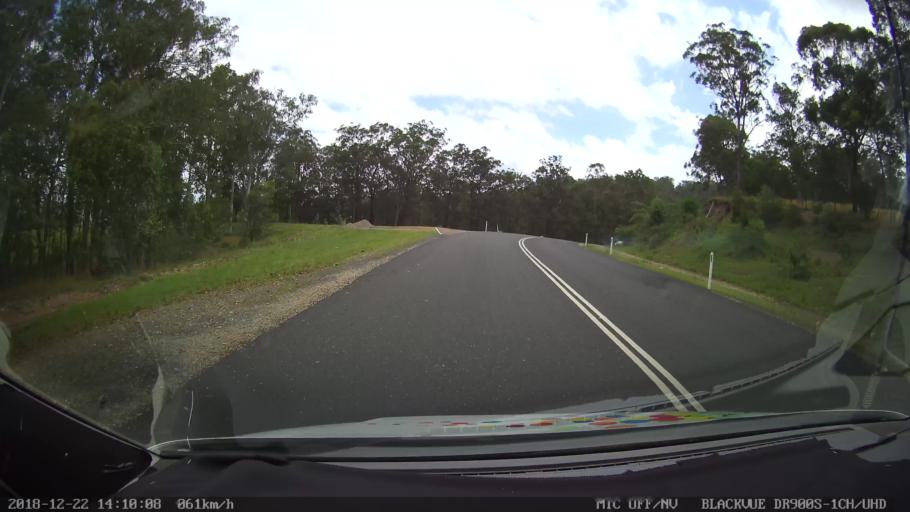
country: AU
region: New South Wales
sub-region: Clarence Valley
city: Coutts Crossing
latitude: -29.9908
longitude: 152.7116
